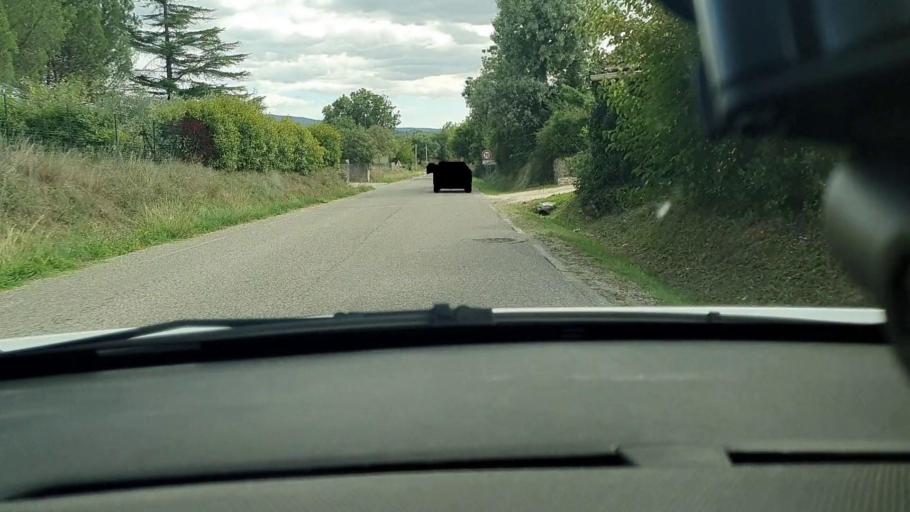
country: FR
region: Languedoc-Roussillon
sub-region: Departement du Gard
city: Les Mages
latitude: 44.2103
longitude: 4.1993
